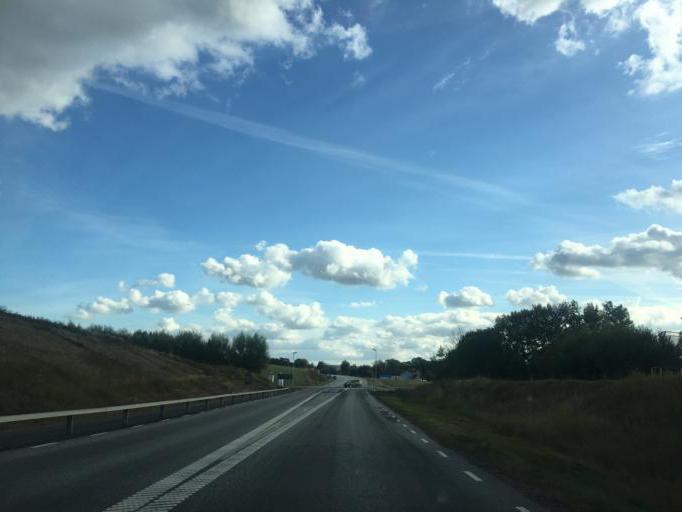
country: SE
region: Skane
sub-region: Eslovs Kommun
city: Eslov
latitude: 55.7663
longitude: 13.3229
